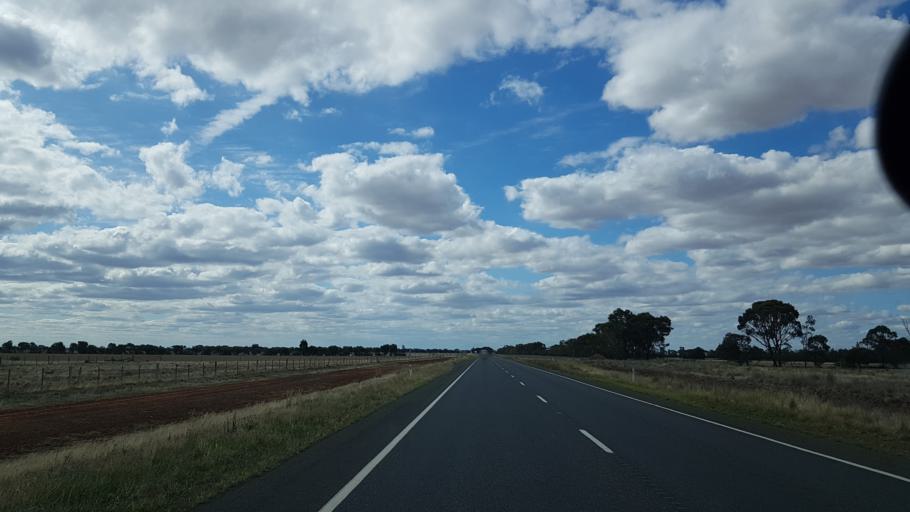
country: AU
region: Victoria
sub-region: Greater Bendigo
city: Long Gully
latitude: -36.0443
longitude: 143.9483
